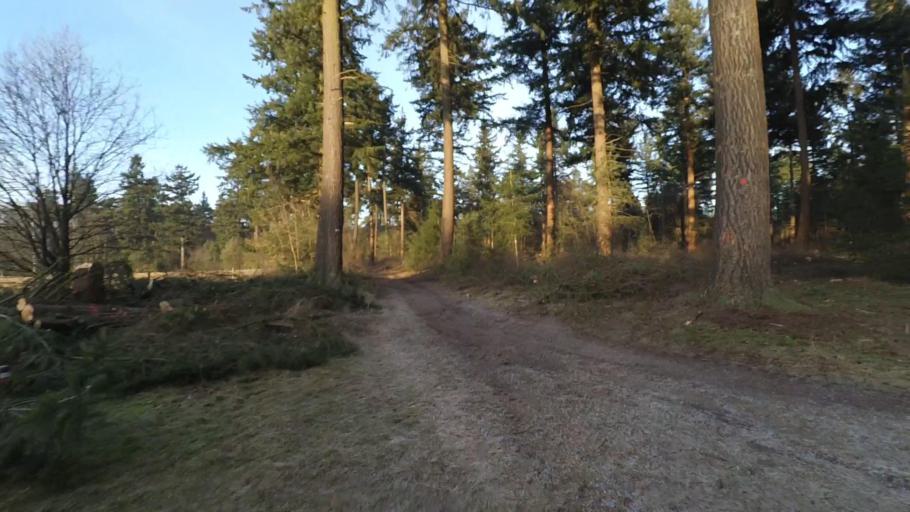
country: NL
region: Utrecht
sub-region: Gemeente Utrechtse Heuvelrug
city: Maarn
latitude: 52.0723
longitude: 5.3544
